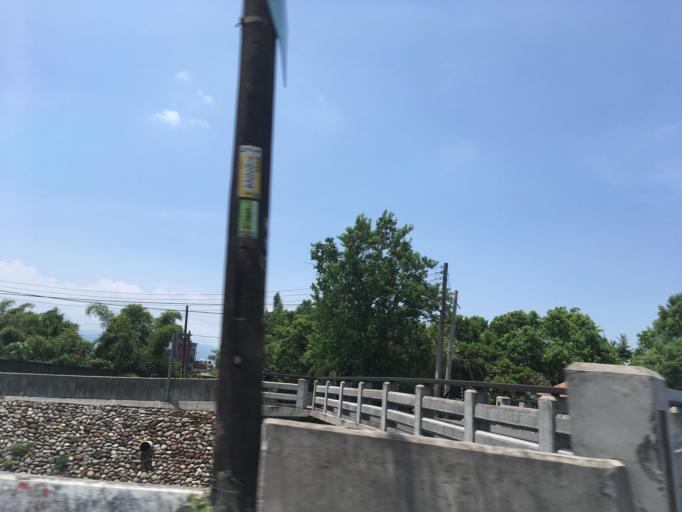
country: TW
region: Taiwan
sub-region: Yilan
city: Yilan
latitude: 24.6422
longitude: 121.7604
